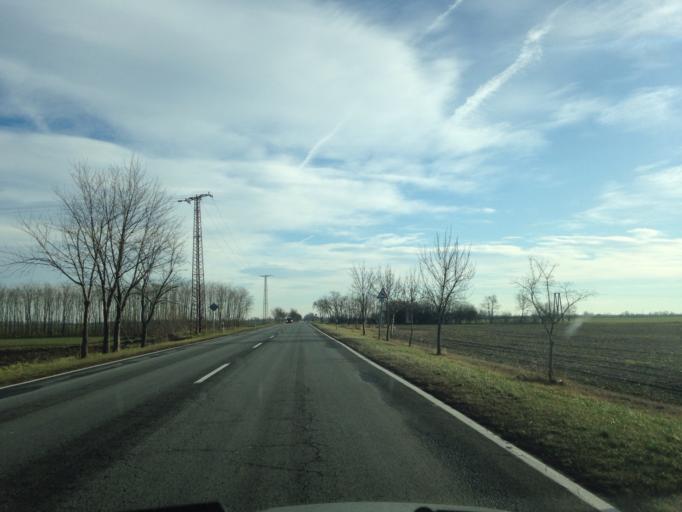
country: HU
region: Gyor-Moson-Sopron
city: Kimle
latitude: 47.8085
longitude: 17.3654
